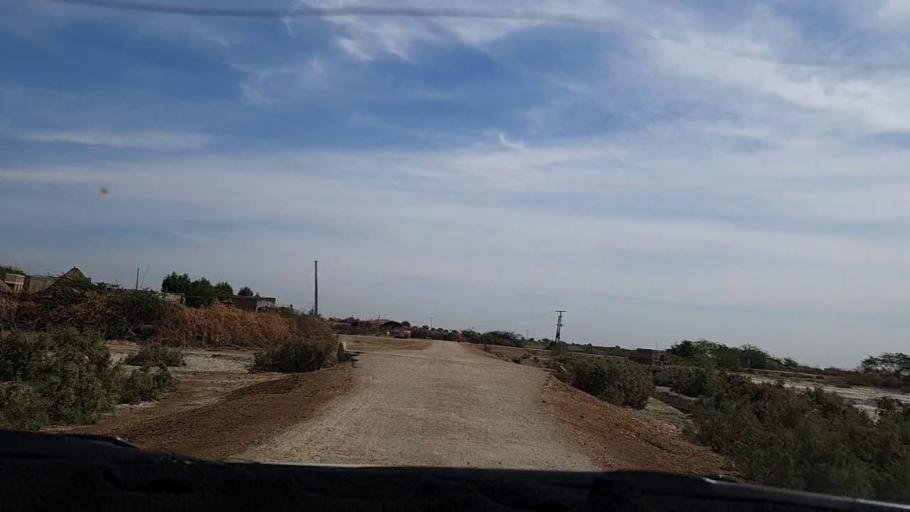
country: PK
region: Sindh
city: Pithoro
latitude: 25.4766
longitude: 69.4570
